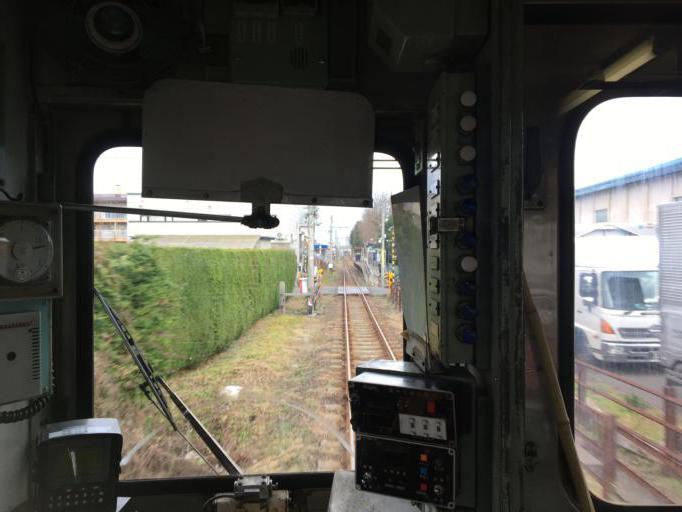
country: JP
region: Aomori
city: Hirosaki
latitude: 40.5764
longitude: 140.4729
